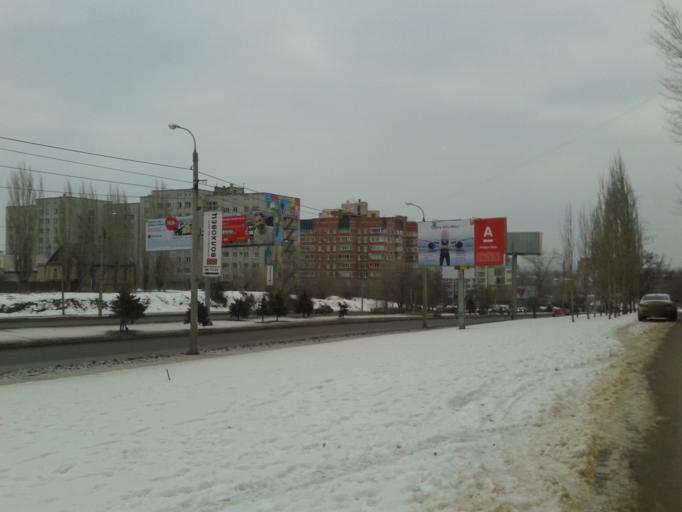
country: RU
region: Volgograd
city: Volgograd
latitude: 48.7268
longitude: 44.5229
